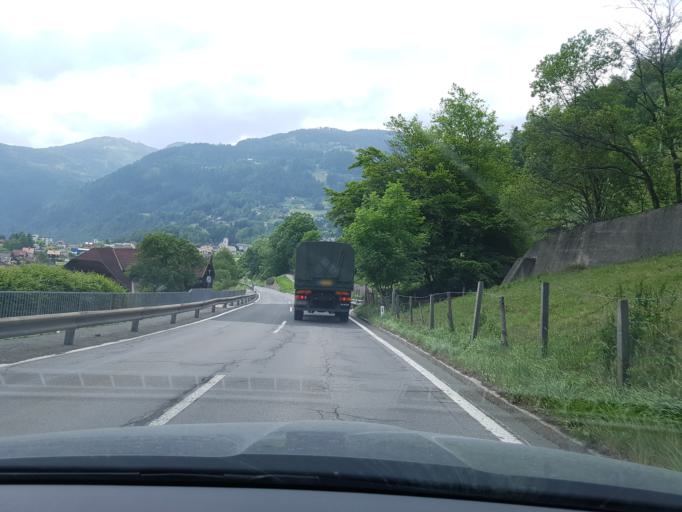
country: AT
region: Carinthia
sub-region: Politischer Bezirk Spittal an der Drau
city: Radenthein
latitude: 46.8009
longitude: 13.7174
